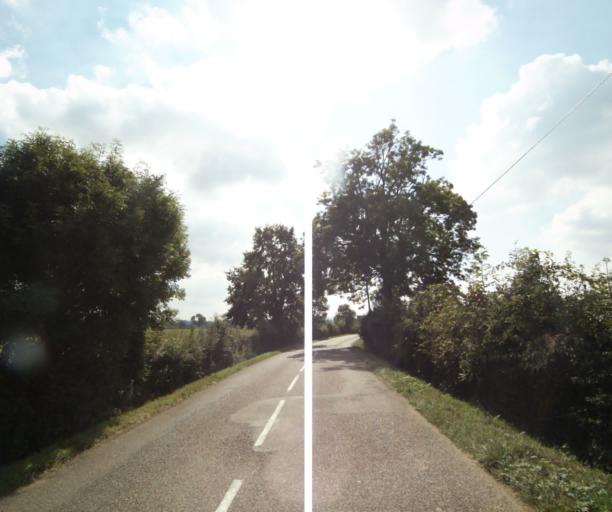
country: FR
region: Bourgogne
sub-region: Departement de Saone-et-Loire
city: Charolles
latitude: 46.3771
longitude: 4.2493
